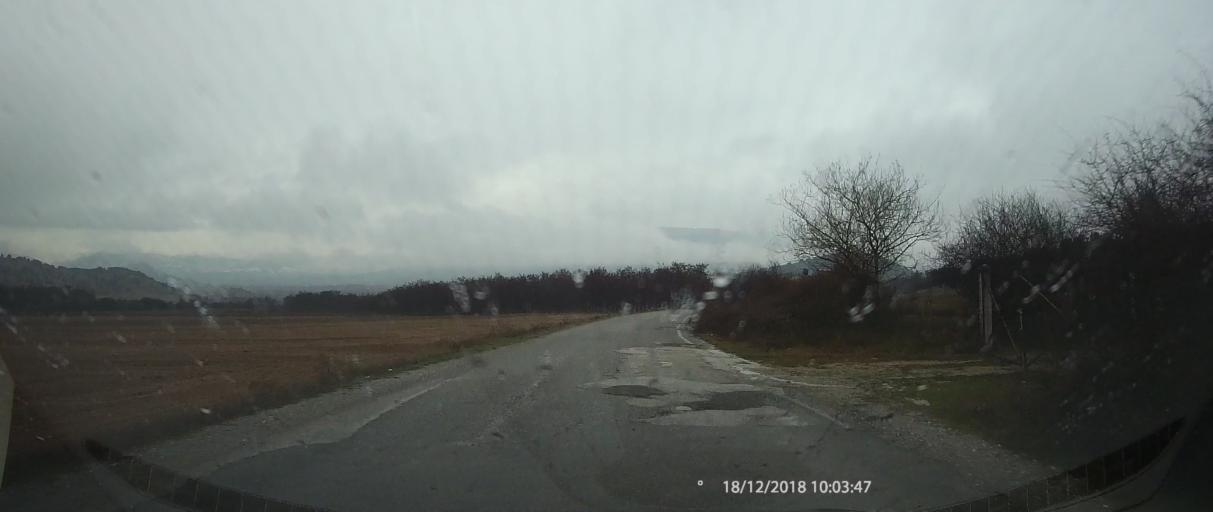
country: GR
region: Thessaly
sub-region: Nomos Larisis
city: Livadi
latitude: 40.0460
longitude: 22.2238
